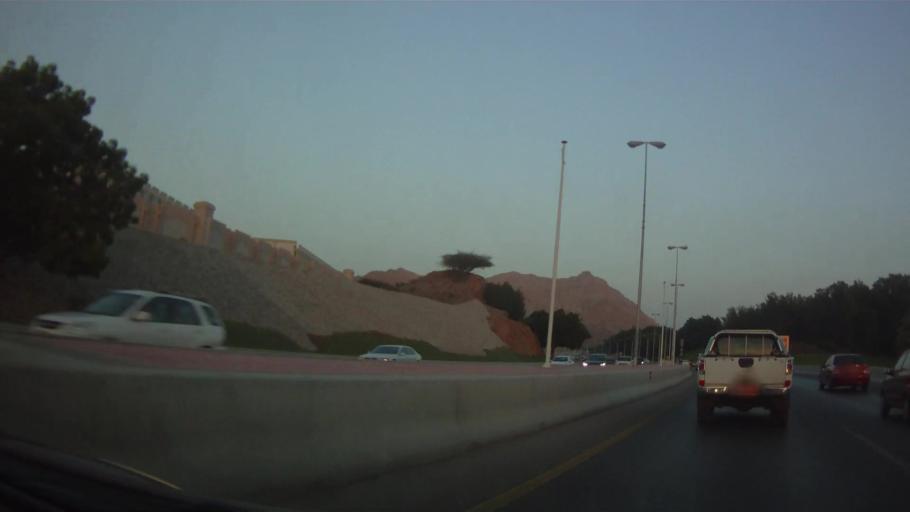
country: OM
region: Muhafazat Masqat
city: Muscat
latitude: 23.6184
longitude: 58.5144
